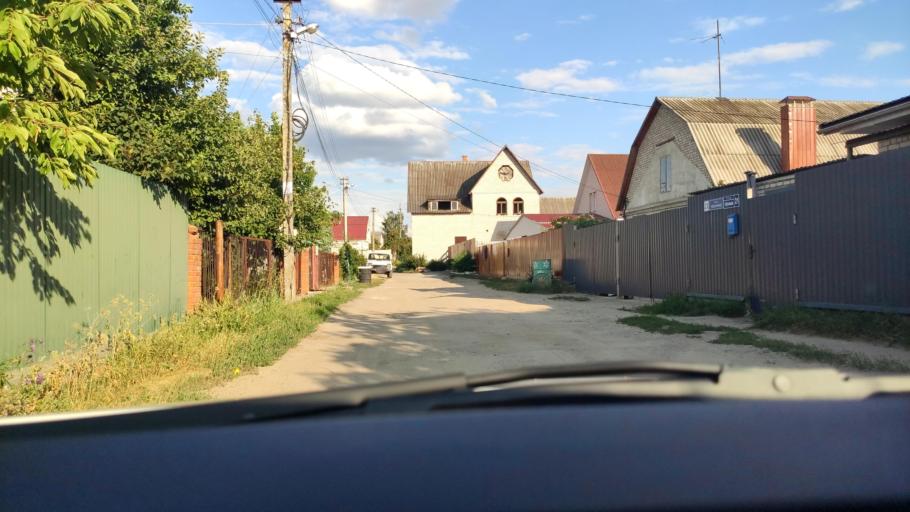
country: RU
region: Voronezj
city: Pridonskoy
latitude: 51.7001
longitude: 39.0833
